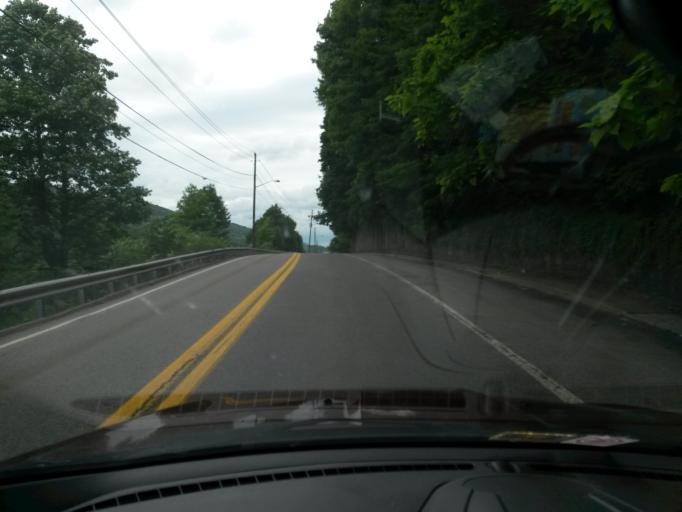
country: US
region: West Virginia
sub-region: Mercer County
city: Bluefield
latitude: 37.2738
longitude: -81.2119
